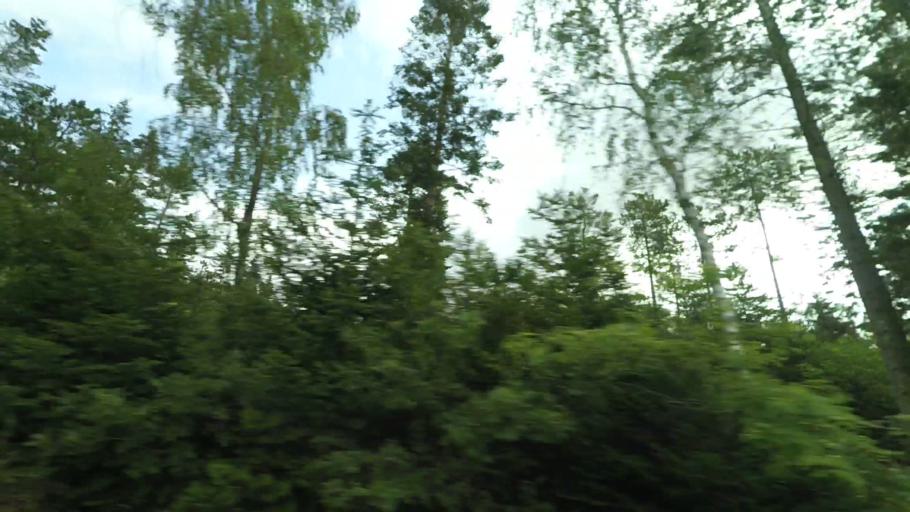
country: DK
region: Central Jutland
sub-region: Syddjurs Kommune
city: Ryomgard
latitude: 56.3584
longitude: 10.5168
